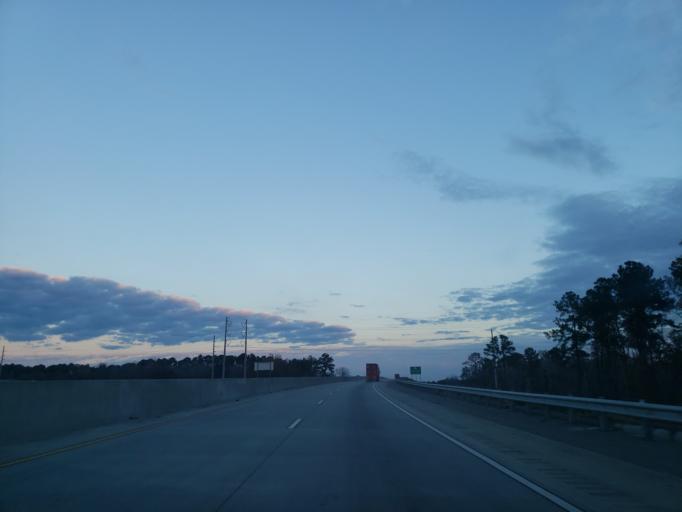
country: US
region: Georgia
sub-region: Chatham County
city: Port Wentworth
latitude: 32.1508
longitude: -81.1753
